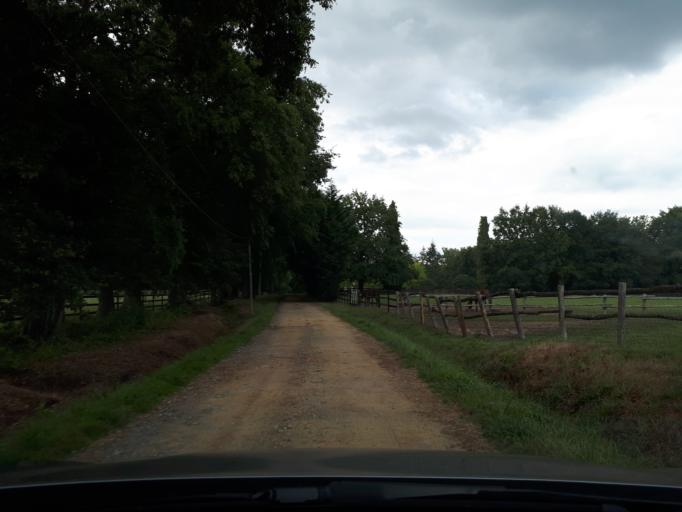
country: FR
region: Pays de la Loire
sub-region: Departement de la Sarthe
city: Champagne
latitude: 48.0568
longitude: 0.3224
